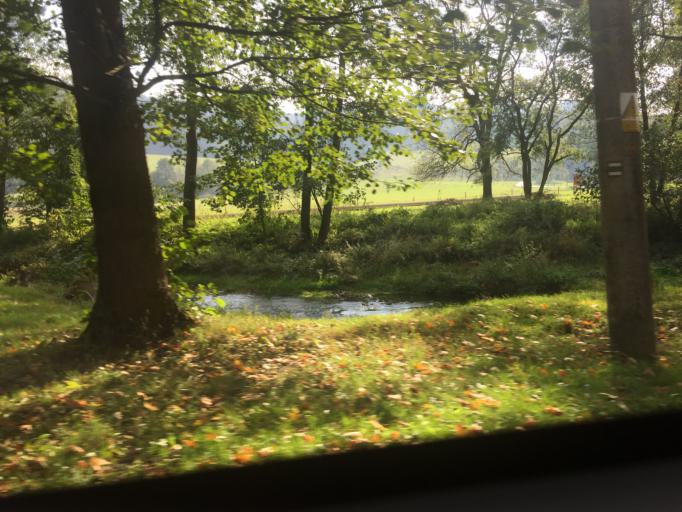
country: CZ
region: Ustecky
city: Ceska Kamenice
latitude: 50.8190
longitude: 14.3521
